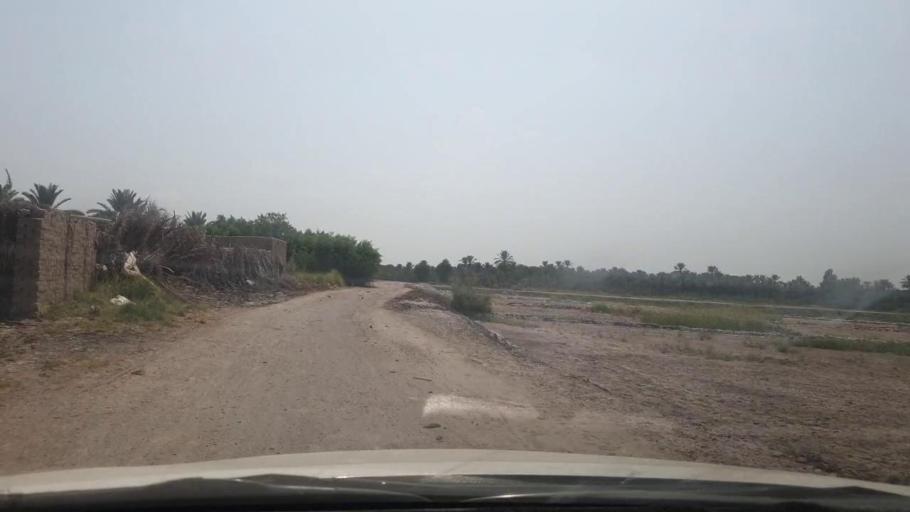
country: PK
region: Sindh
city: Khairpur
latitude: 27.5644
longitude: 68.8441
